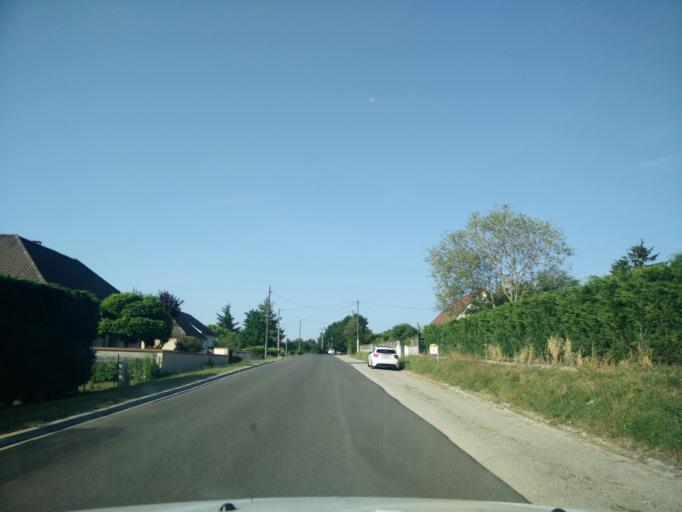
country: FR
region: Auvergne
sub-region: Departement de l'Allier
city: Toulon-sur-Allier
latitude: 46.4867
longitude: 3.3105
